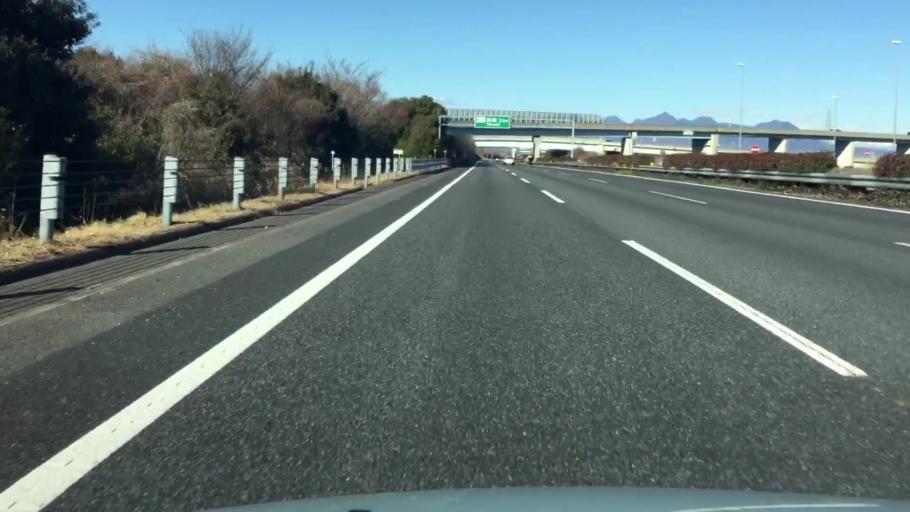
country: JP
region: Gunma
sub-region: Sawa-gun
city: Tamamura
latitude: 36.3195
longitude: 139.0777
